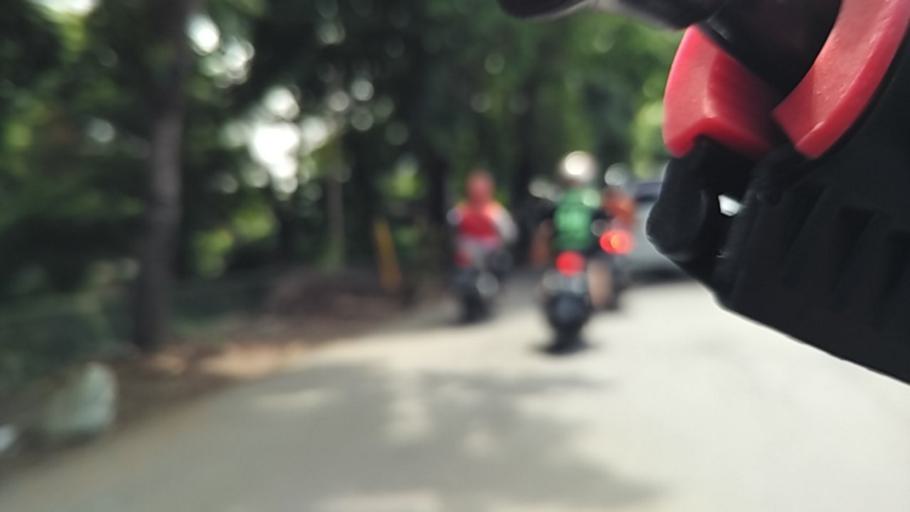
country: ID
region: Central Java
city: Semarang
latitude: -6.9980
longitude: 110.4210
